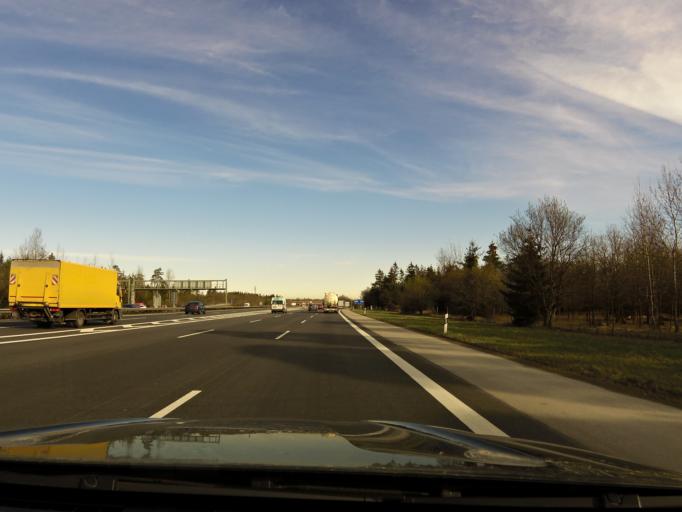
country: DE
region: Bavaria
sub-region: Upper Bavaria
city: Brunnthal
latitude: 48.0142
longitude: 11.6654
